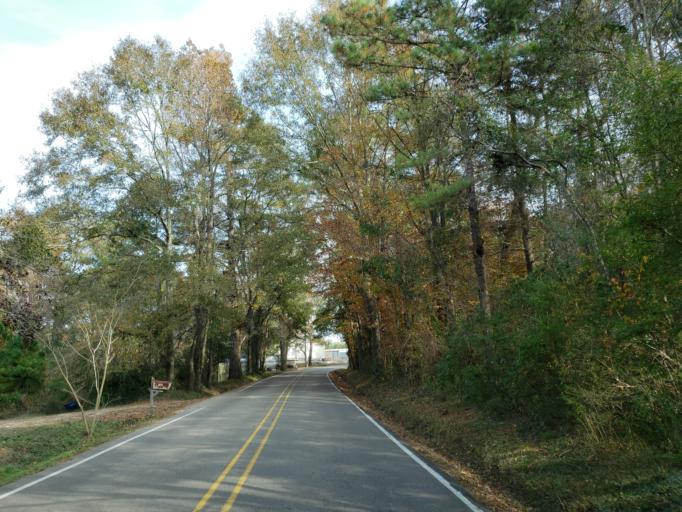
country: US
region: Mississippi
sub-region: Forrest County
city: Rawls Springs
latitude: 31.3869
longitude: -89.3772
